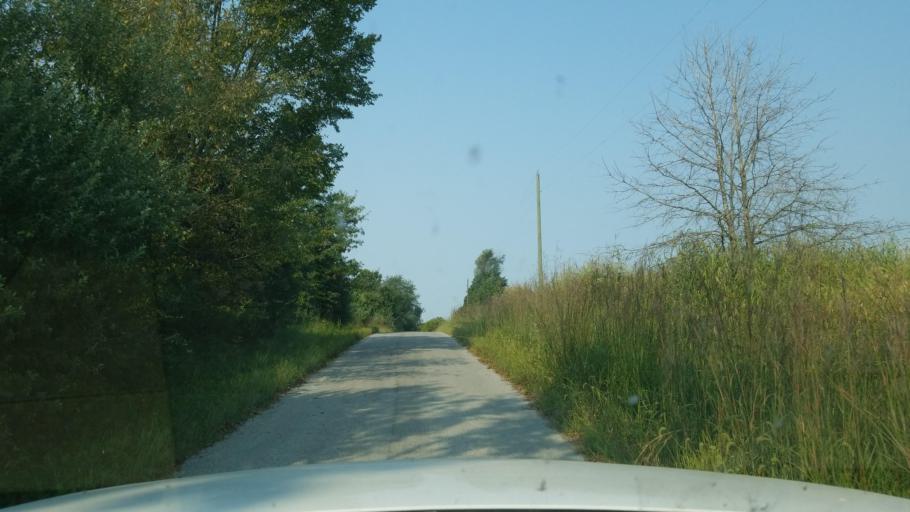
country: US
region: Illinois
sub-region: Saline County
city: Carrier Mills
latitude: 37.7904
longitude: -88.6996
